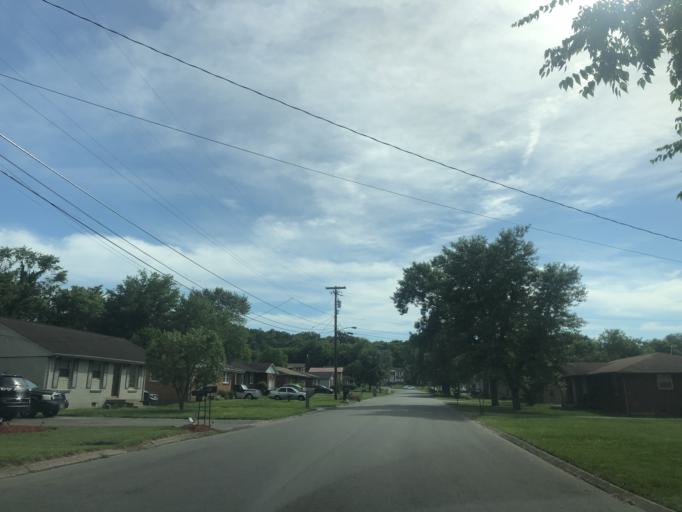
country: US
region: Tennessee
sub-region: Davidson County
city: Nashville
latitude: 36.2166
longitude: -86.8149
